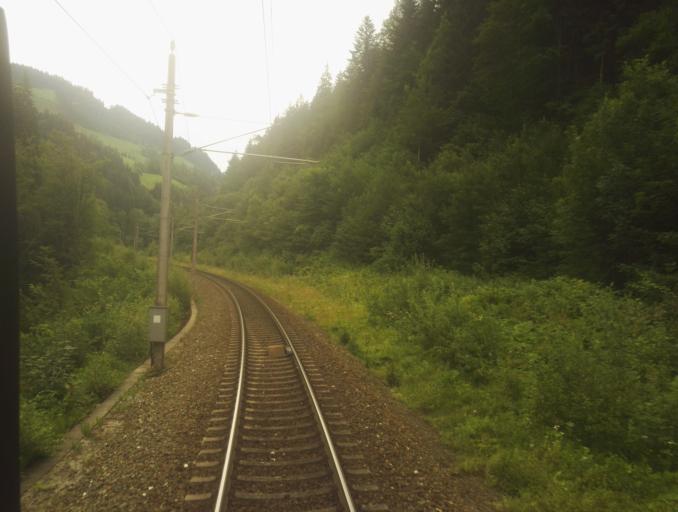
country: AT
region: Salzburg
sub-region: Politischer Bezirk Sankt Johann im Pongau
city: Huttau
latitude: 47.4245
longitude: 13.2865
